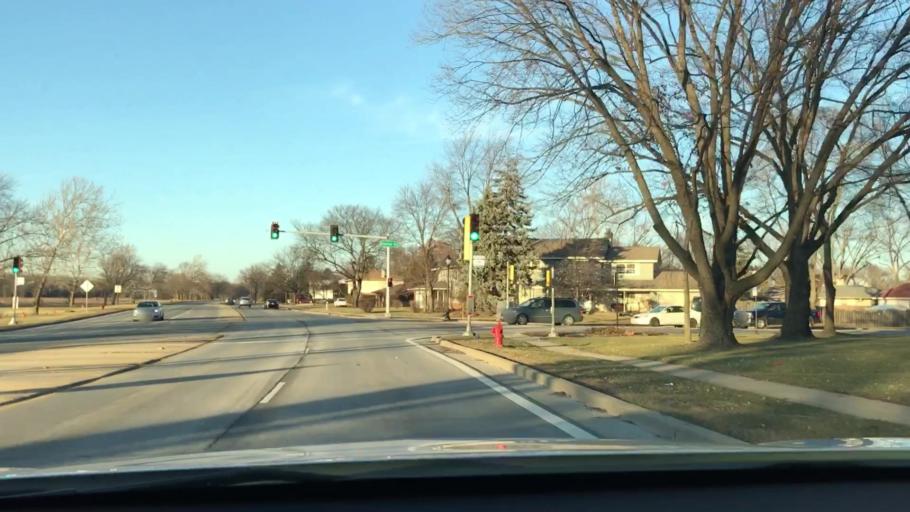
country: US
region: Illinois
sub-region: Cook County
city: Elk Grove Village
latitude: 42.0216
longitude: -87.9883
